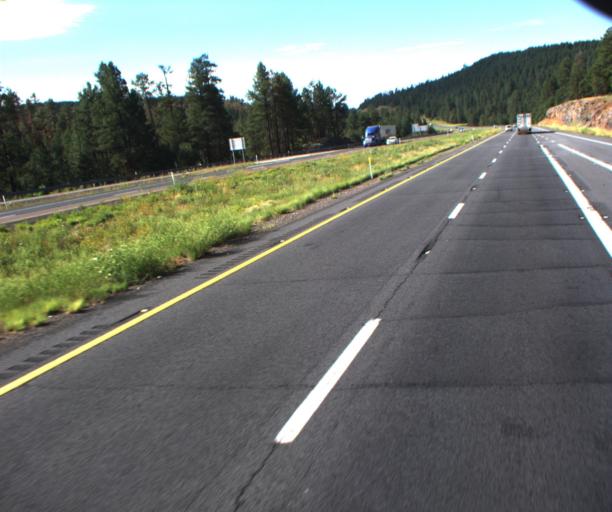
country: US
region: Arizona
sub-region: Coconino County
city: Mountainaire
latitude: 35.0480
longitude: -111.6840
